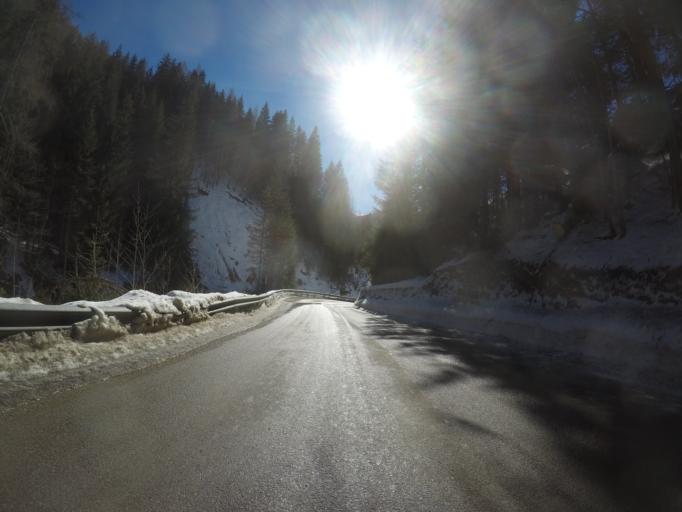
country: IT
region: Veneto
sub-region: Provincia di Belluno
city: Colle Santa Lucia
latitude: 46.4609
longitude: 12.0319
